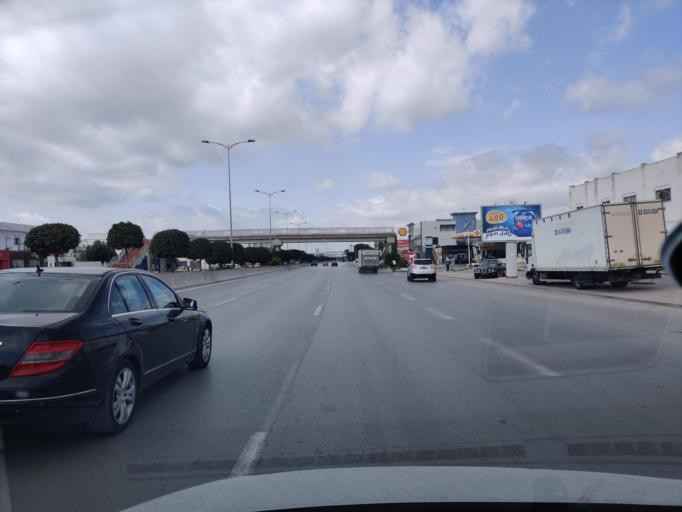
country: TN
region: Tunis
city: Al Marsa
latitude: 36.8679
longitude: 10.3066
